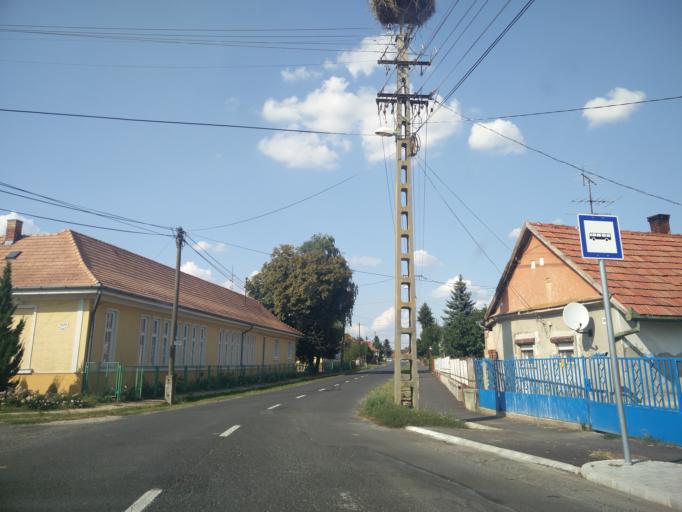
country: HU
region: Zala
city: Zalaegerszeg
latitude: 46.8744
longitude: 16.8239
